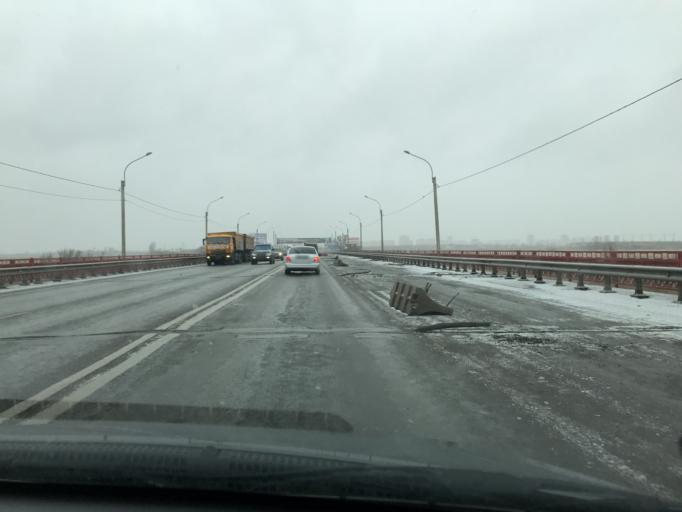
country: RU
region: Rostov
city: Bataysk
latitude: 47.1770
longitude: 39.7415
